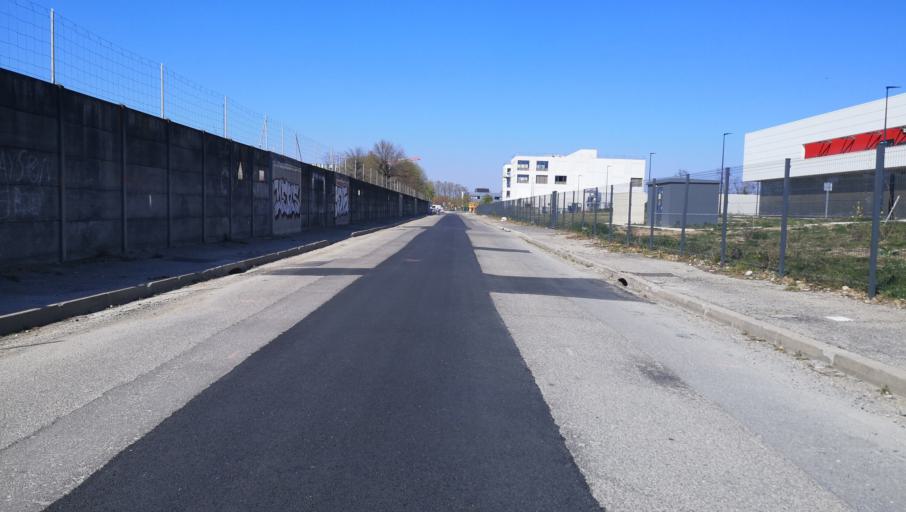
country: FR
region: Rhone-Alpes
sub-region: Departement du Rhone
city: Saint-Fons
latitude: 45.7197
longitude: 4.8458
